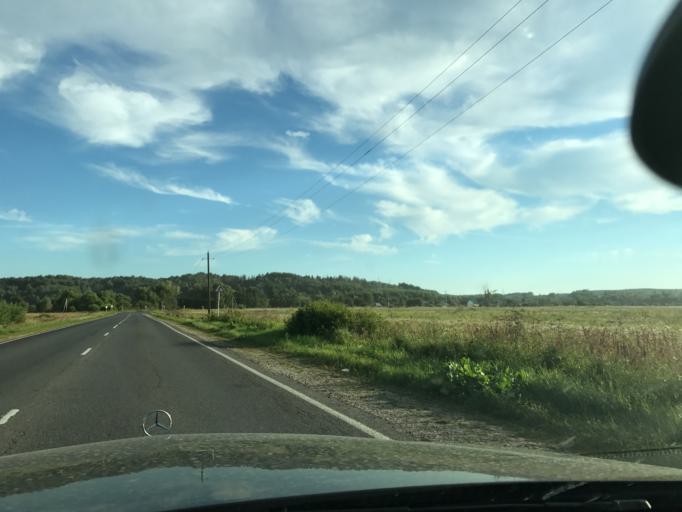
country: RU
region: Vladimir
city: Raduzhnyy
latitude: 56.0269
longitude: 40.3371
